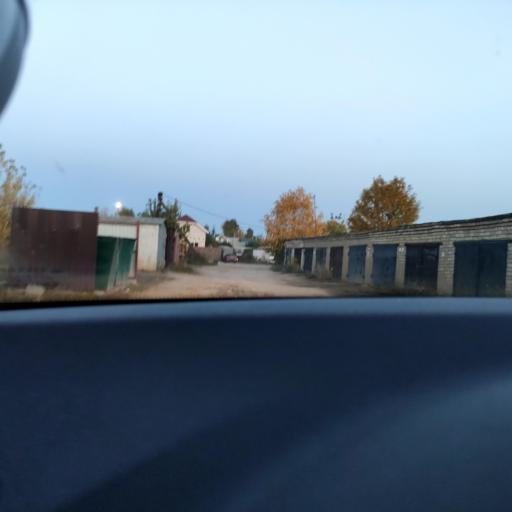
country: RU
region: Samara
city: Novosemeykino
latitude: 53.3690
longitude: 50.3523
